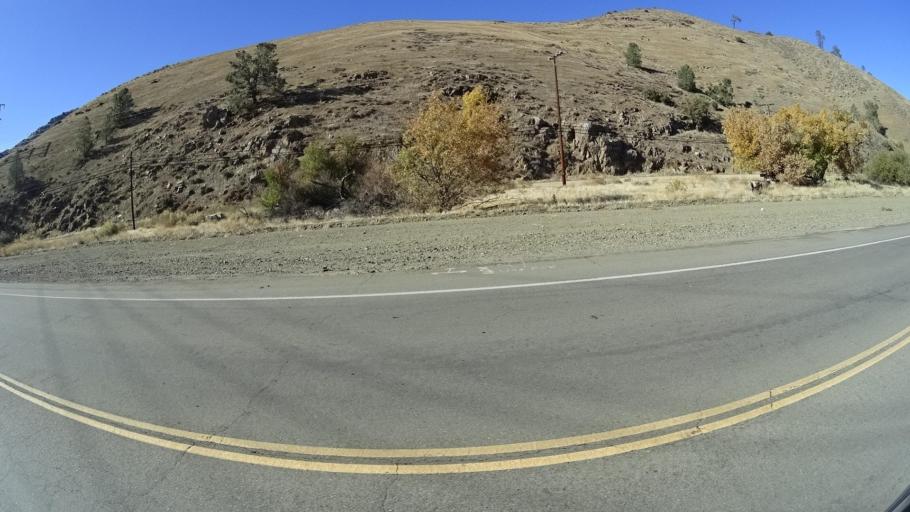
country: US
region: California
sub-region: Kern County
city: Kernville
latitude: 35.7433
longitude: -118.4237
